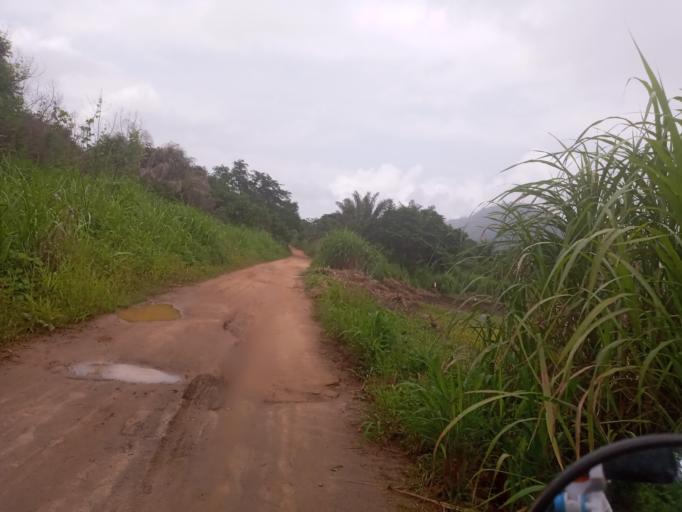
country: SL
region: Northern Province
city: Bumbuna
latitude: 8.9598
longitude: -11.7586
